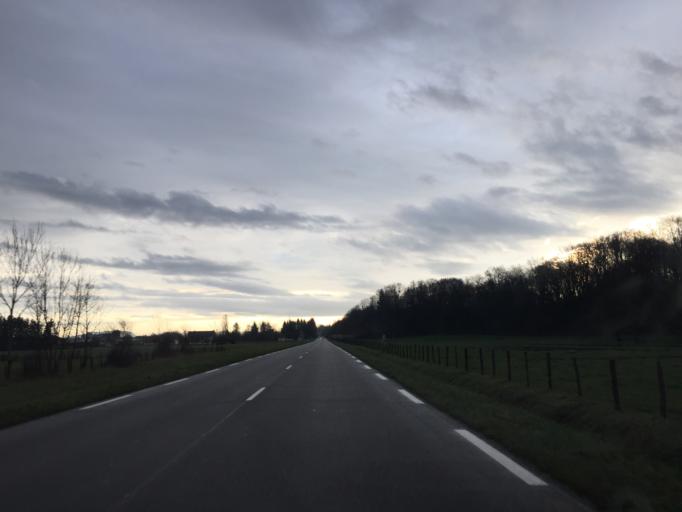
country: FR
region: Franche-Comte
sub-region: Departement du Jura
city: Mont-sous-Vaudrey
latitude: 46.9990
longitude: 5.5357
